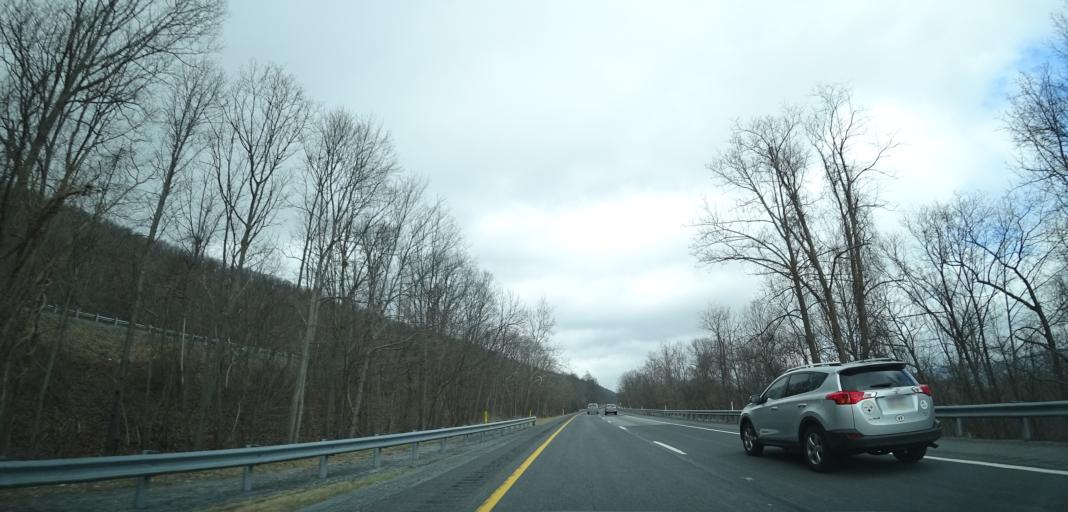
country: US
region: Maryland
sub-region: Washington County
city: Hancock
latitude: 39.8427
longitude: -78.2753
